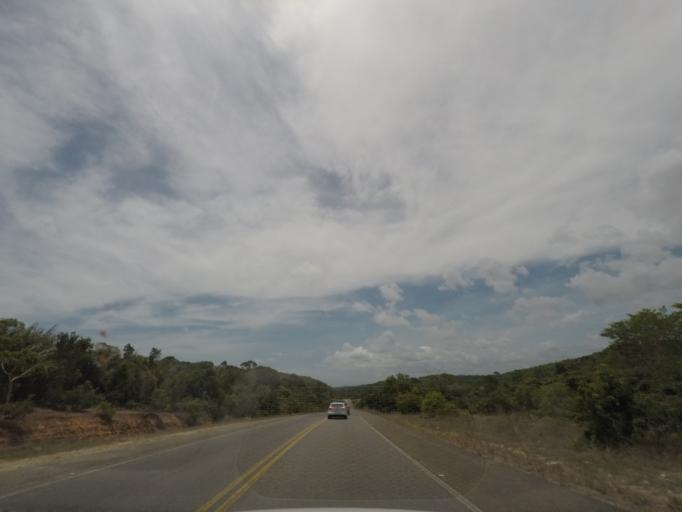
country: BR
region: Bahia
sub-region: Conde
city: Conde
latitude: -12.0220
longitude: -37.6923
